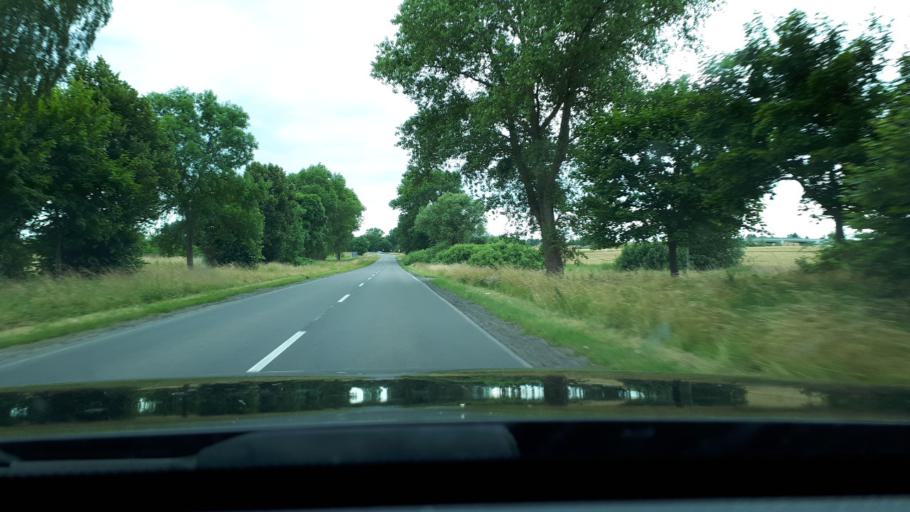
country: PL
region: Warmian-Masurian Voivodeship
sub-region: Powiat olsztynski
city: Olsztynek
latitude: 53.5693
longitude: 20.2697
